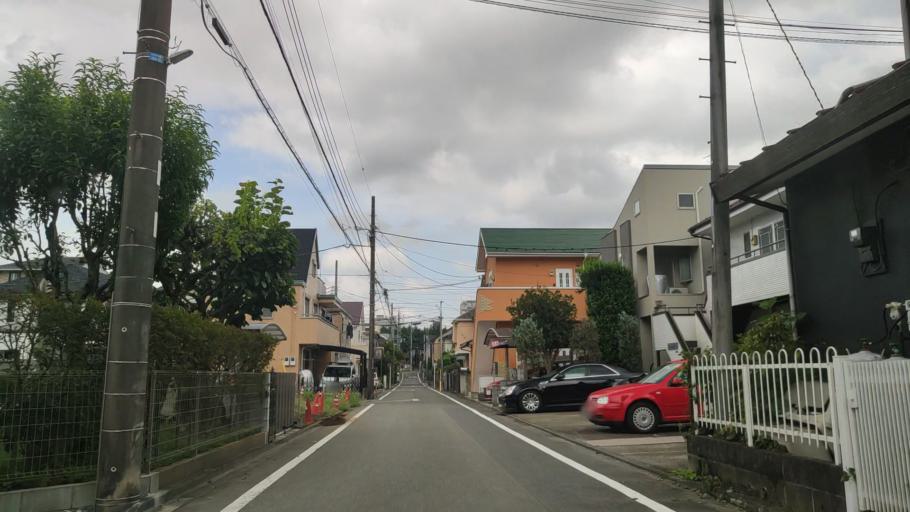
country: JP
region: Kanagawa
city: Minami-rinkan
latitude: 35.5095
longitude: 139.4390
